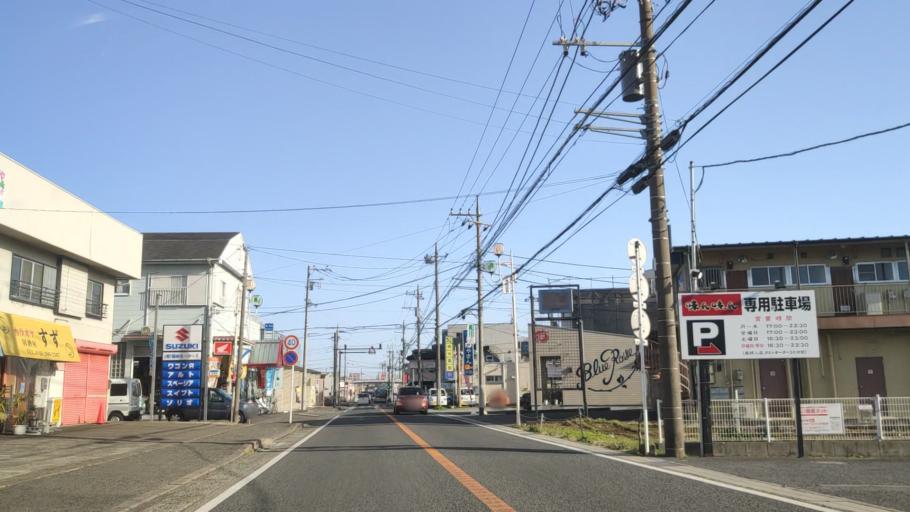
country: JP
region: Kanagawa
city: Zama
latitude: 35.5150
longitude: 139.3355
